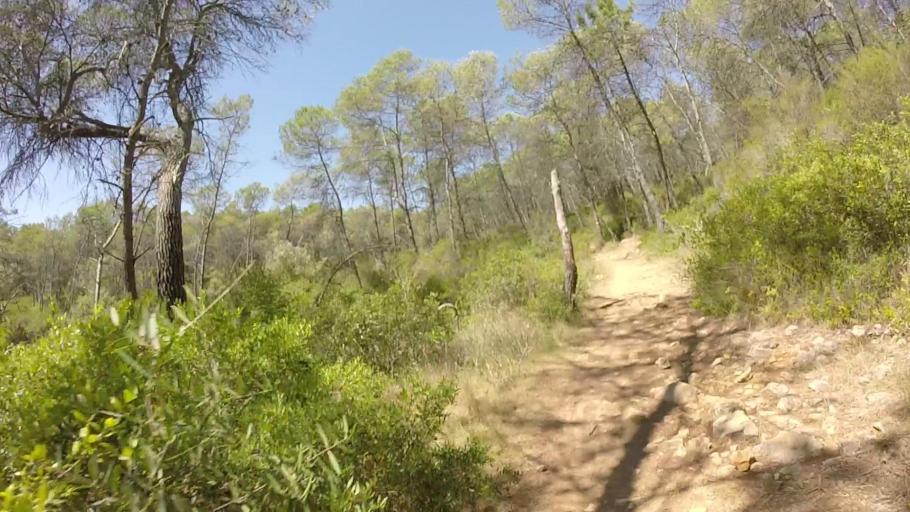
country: FR
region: Provence-Alpes-Cote d'Azur
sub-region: Departement des Alpes-Maritimes
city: Vallauris
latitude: 43.6077
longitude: 7.0486
